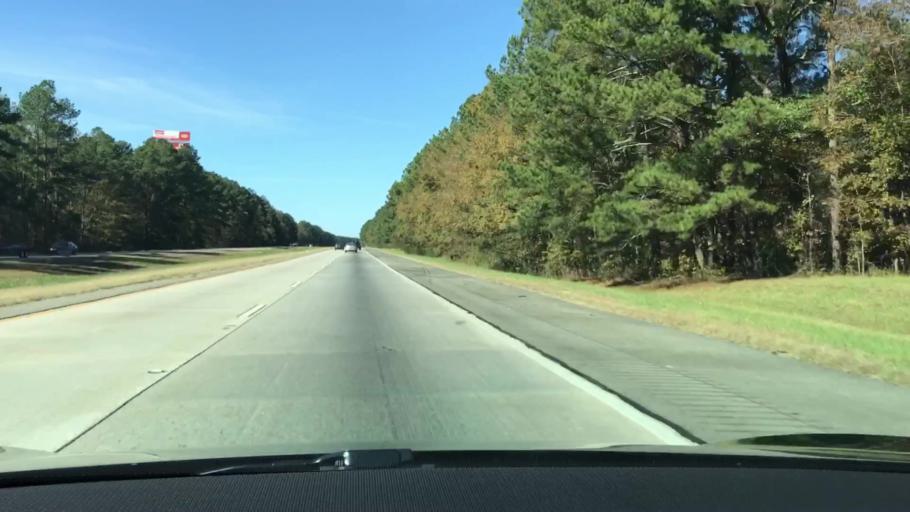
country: US
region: Georgia
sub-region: Taliaferro County
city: Crawfordville
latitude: 33.5295
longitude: -82.9681
